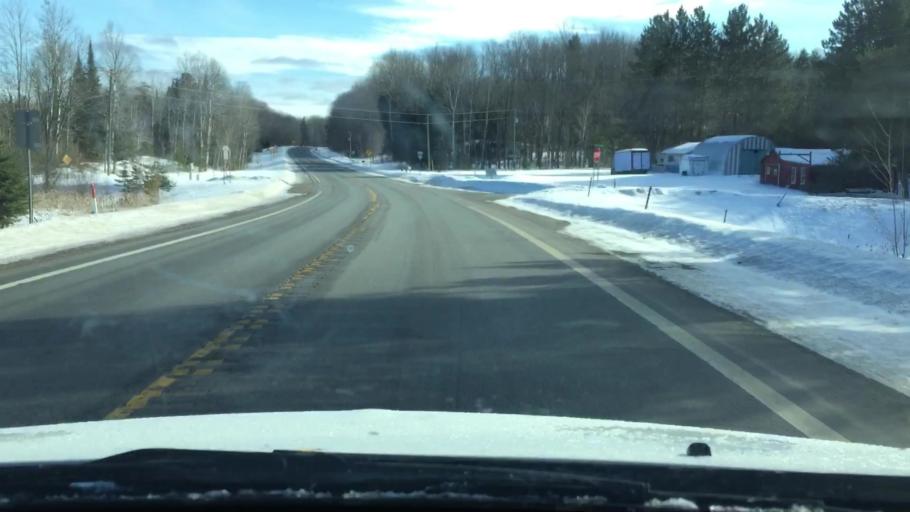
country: US
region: Michigan
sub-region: Antrim County
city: Mancelona
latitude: 44.9897
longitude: -85.0604
